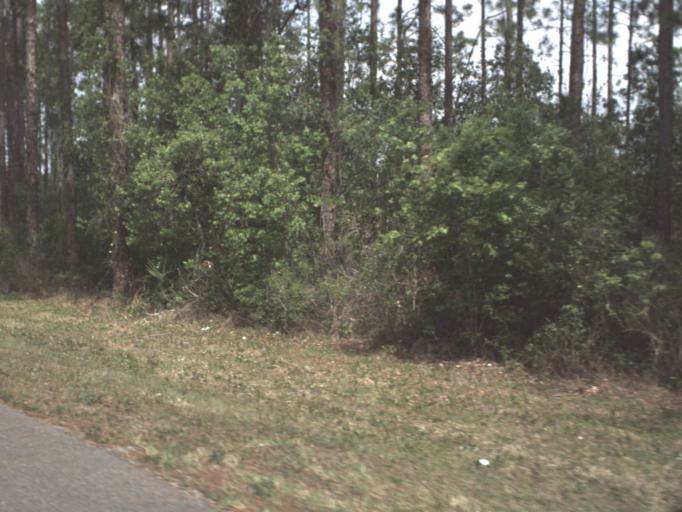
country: US
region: Florida
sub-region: Volusia County
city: Pierson
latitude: 29.2809
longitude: -81.3319
